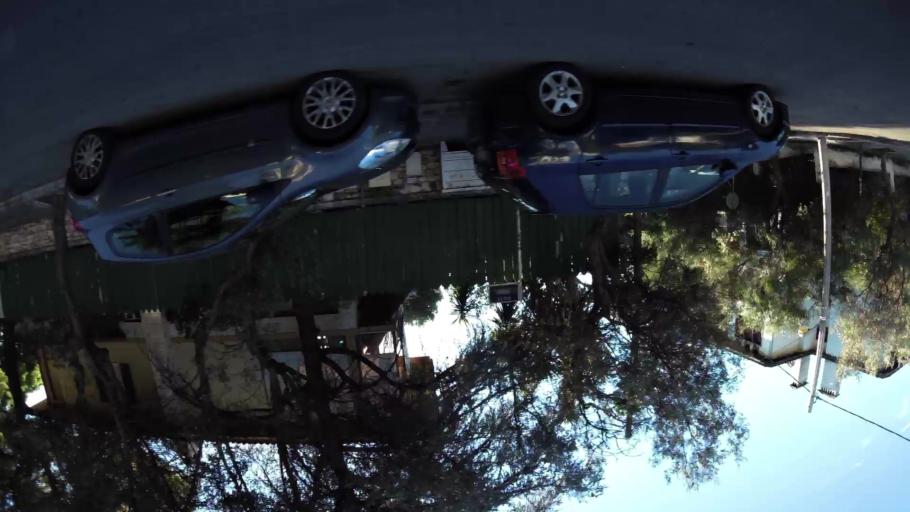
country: GR
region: Attica
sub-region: Nomarchia Athinas
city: Nea Erythraia
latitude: 38.0858
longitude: 23.8298
